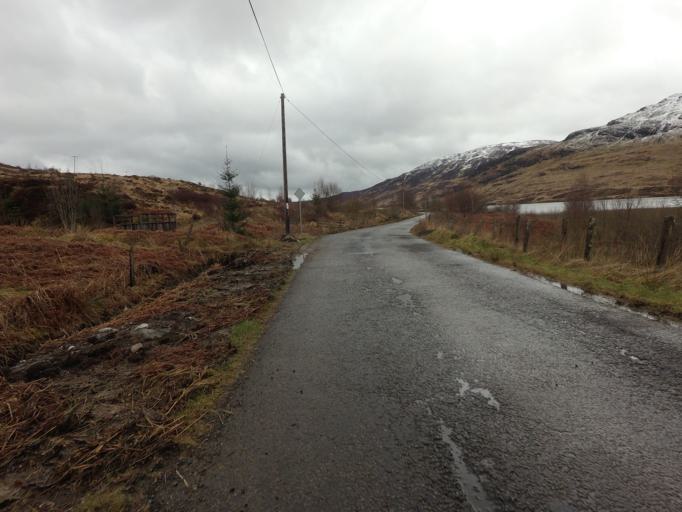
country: GB
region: Scotland
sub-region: Argyll and Bute
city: Garelochhead
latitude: 56.2495
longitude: -4.6455
